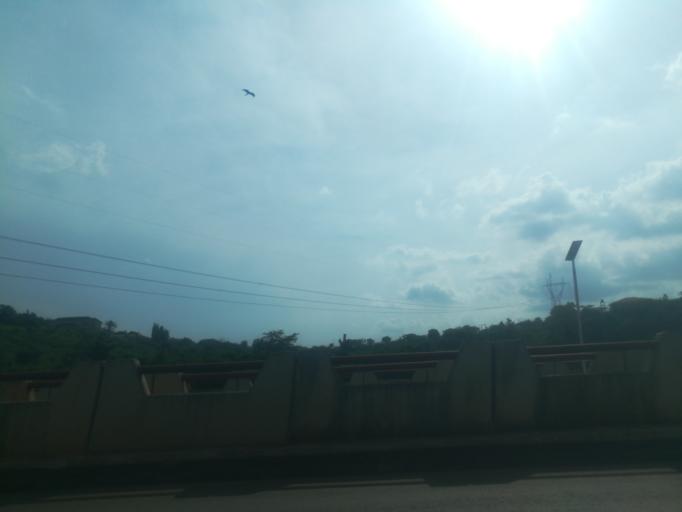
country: NG
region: Ogun
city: Abeokuta
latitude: 7.1253
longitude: 3.3581
